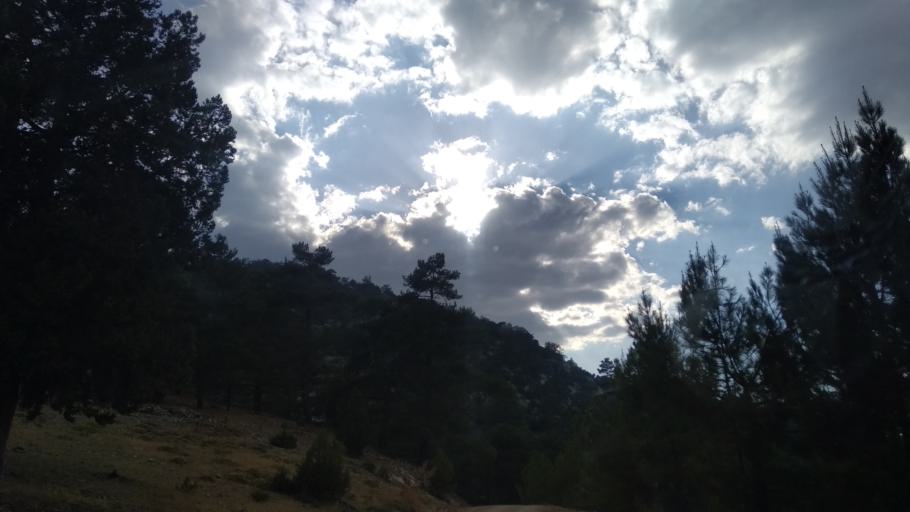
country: TR
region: Mersin
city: Sarikavak
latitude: 36.5977
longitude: 33.7067
